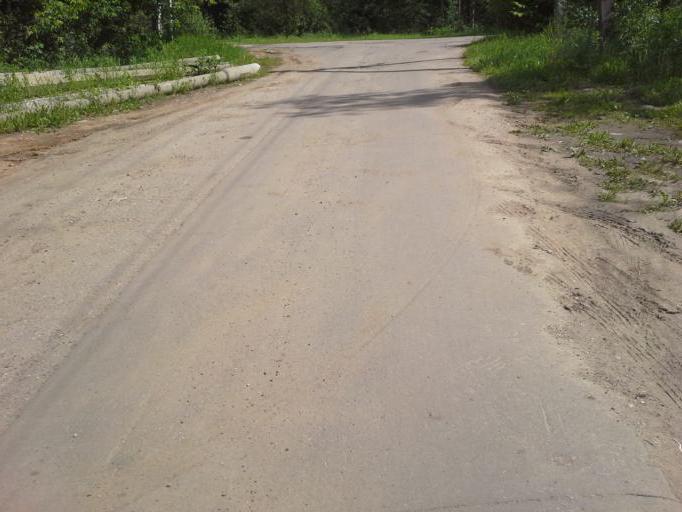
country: RU
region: Moscow
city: Tolstopal'tsevo
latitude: 55.6223
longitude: 37.2157
